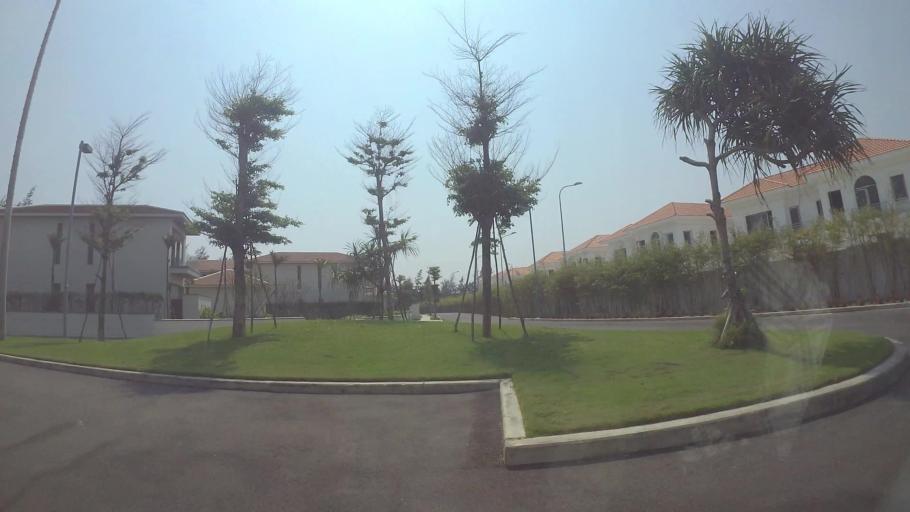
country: VN
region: Da Nang
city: Ngu Hanh Son
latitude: 15.9805
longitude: 108.2806
